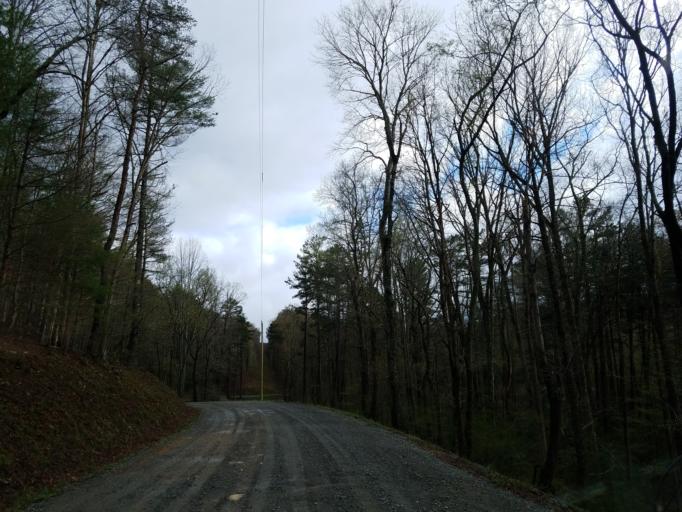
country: US
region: Georgia
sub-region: Fannin County
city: Blue Ridge
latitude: 34.8074
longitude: -84.2457
